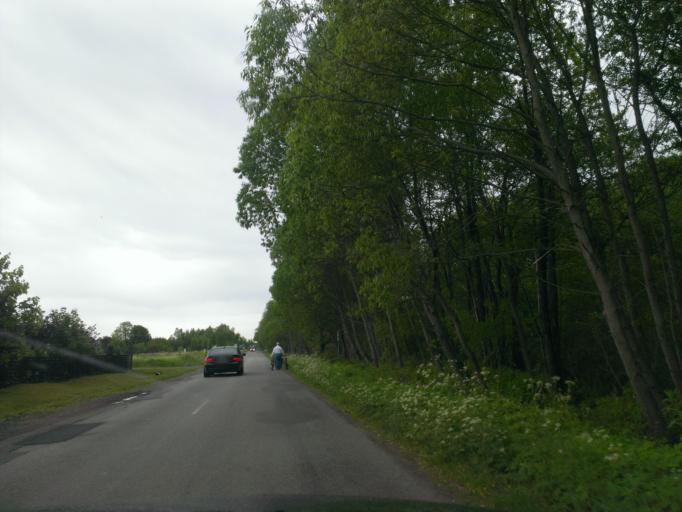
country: LT
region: Klaipedos apskritis
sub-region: Klaipeda
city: Klaipeda
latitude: 55.8100
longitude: 21.0727
